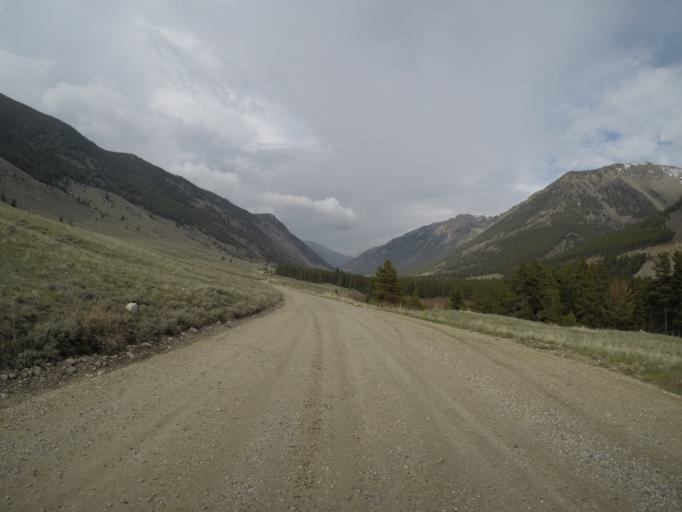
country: US
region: Montana
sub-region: Carbon County
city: Red Lodge
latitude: 45.0543
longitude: -109.4185
